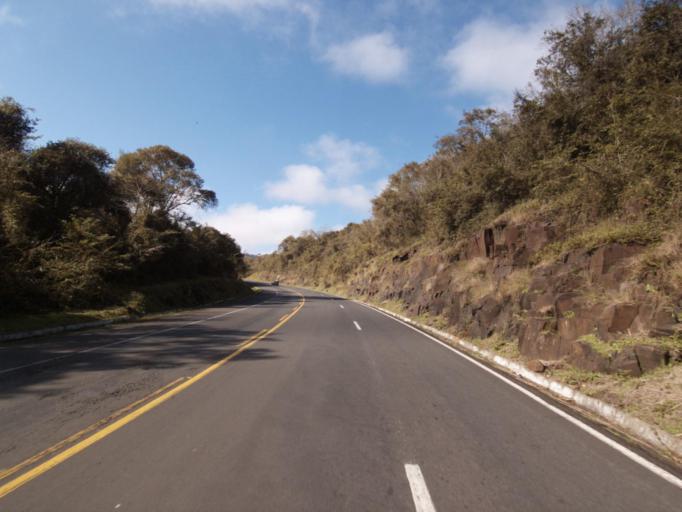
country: BR
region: Rio Grande do Sul
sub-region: Frederico Westphalen
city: Frederico Westphalen
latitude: -27.0830
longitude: -53.2228
